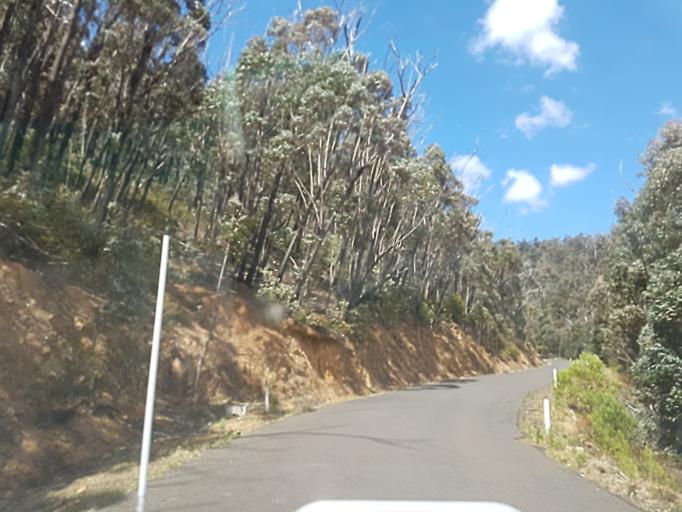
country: AU
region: Victoria
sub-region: East Gippsland
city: Bairnsdale
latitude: -37.3859
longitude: 147.2230
